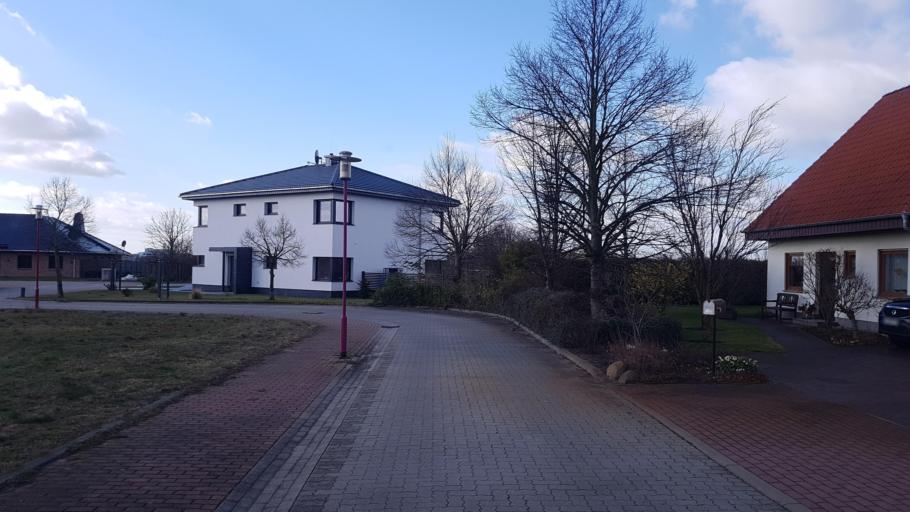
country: DE
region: Brandenburg
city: Herzberg
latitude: 51.6918
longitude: 13.2186
